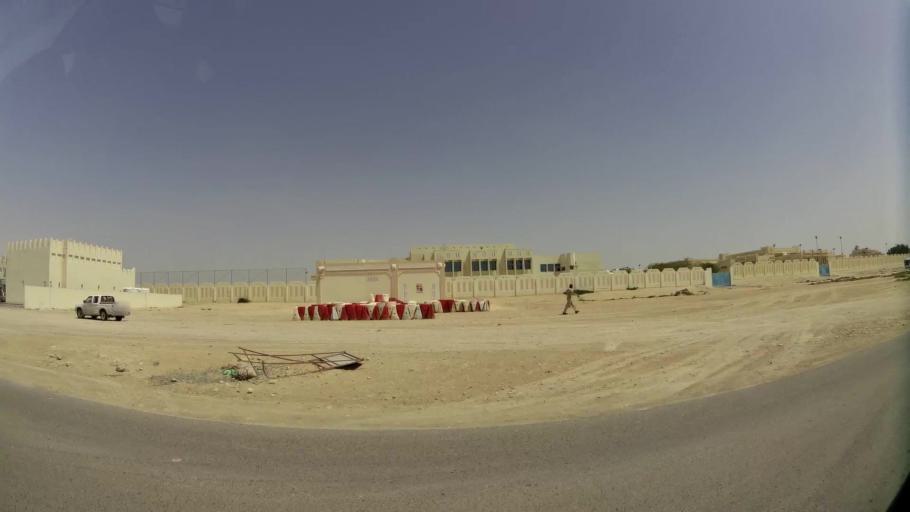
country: QA
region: Baladiyat Umm Salal
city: Umm Salal Muhammad
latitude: 25.3956
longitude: 51.4448
